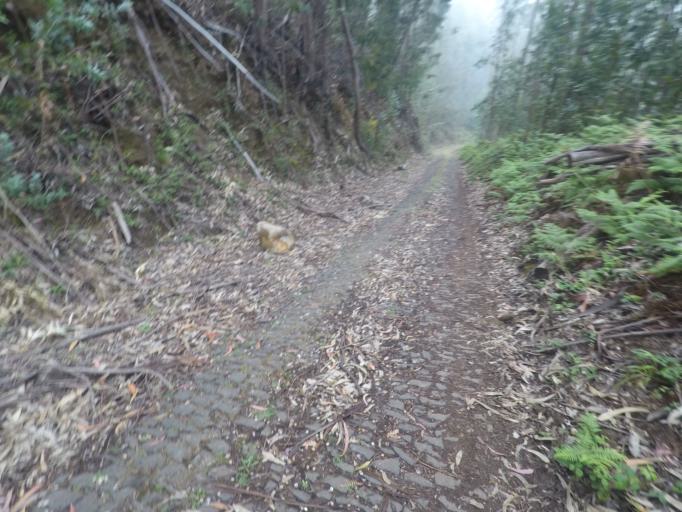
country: PT
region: Madeira
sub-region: Calheta
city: Arco da Calheta
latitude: 32.7300
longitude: -17.0967
